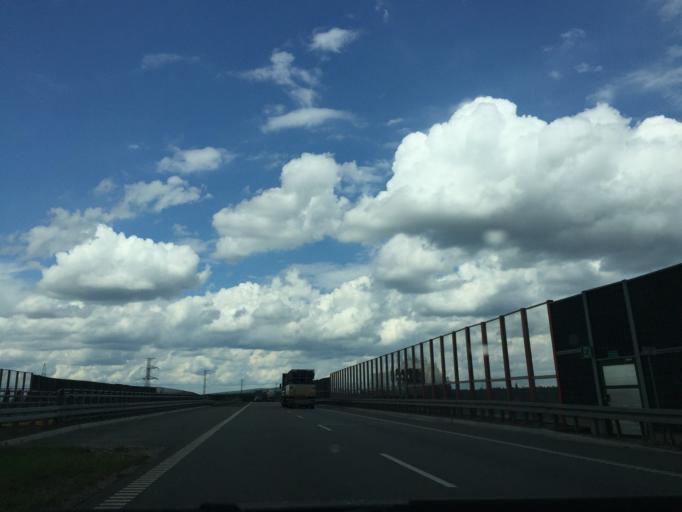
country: PL
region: Swietokrzyskie
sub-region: Powiat kielecki
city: Piekoszow
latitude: 50.8815
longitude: 20.5217
